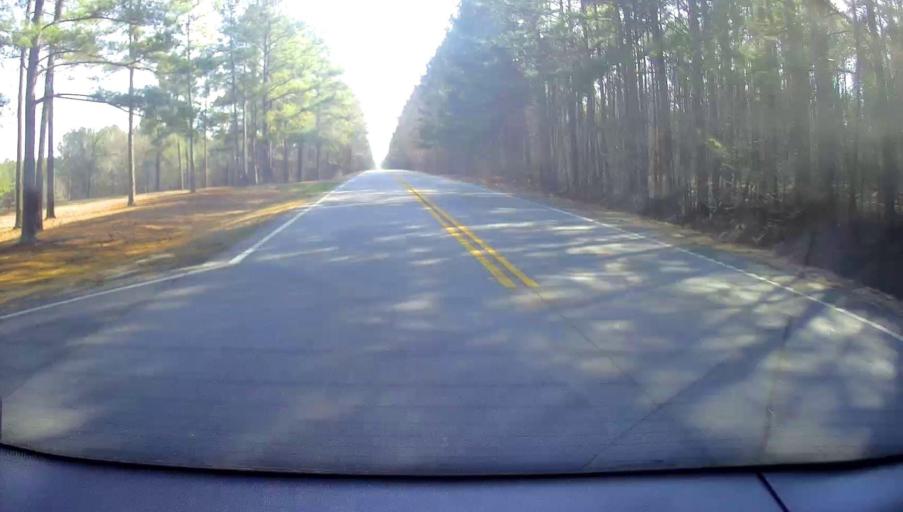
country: US
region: Georgia
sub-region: Butts County
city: Indian Springs
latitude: 33.1597
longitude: -83.8406
